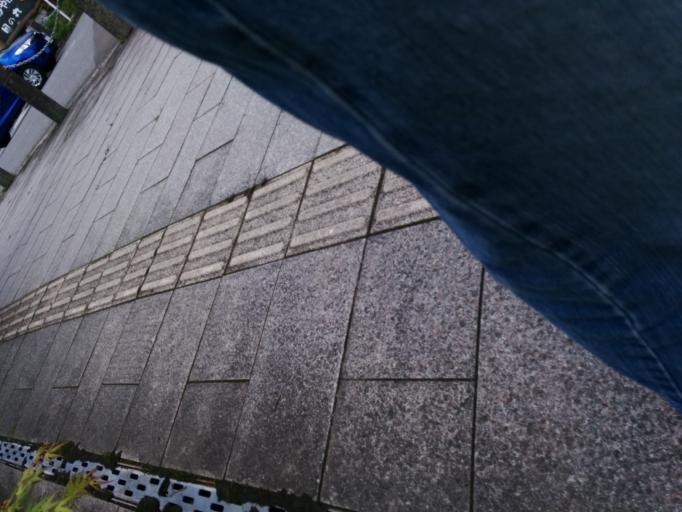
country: JP
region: Tochigi
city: Nikko
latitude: 36.7535
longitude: 139.5987
